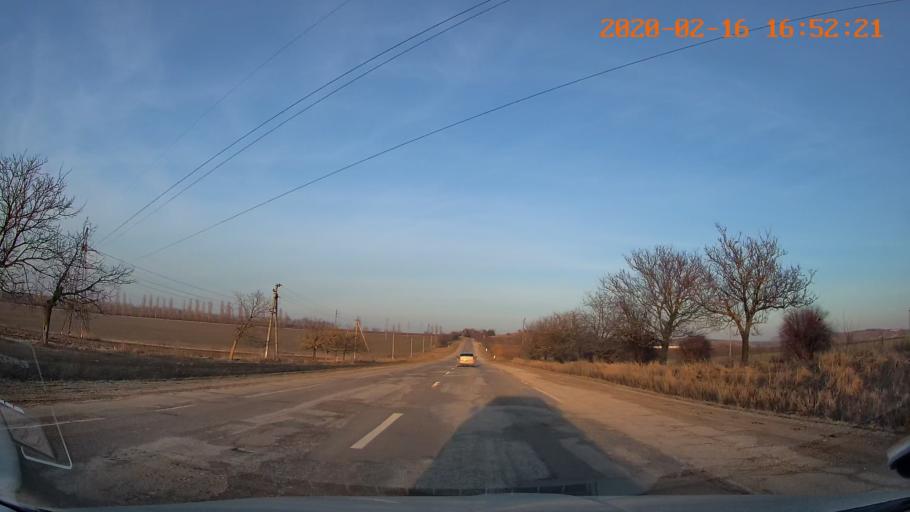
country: MD
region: Briceni
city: Briceni
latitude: 48.3122
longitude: 26.9599
